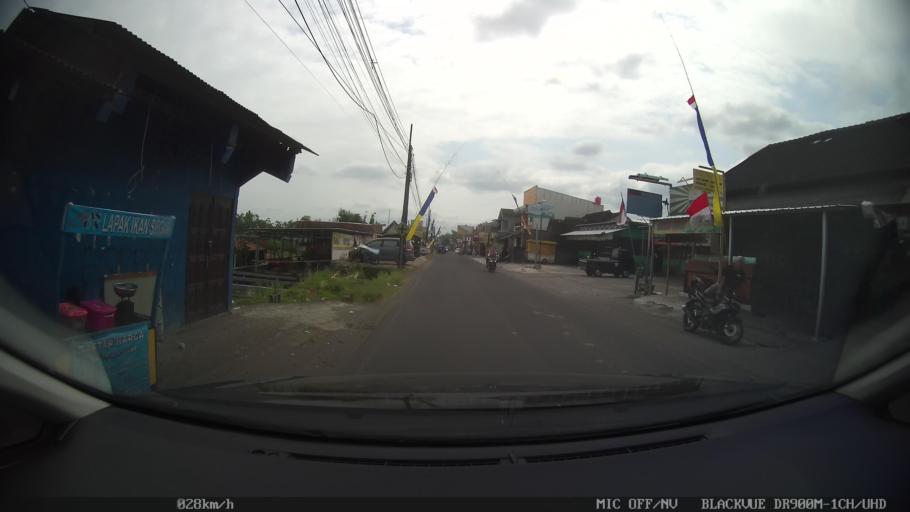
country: ID
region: Daerah Istimewa Yogyakarta
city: Depok
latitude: -7.7534
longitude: 110.4457
